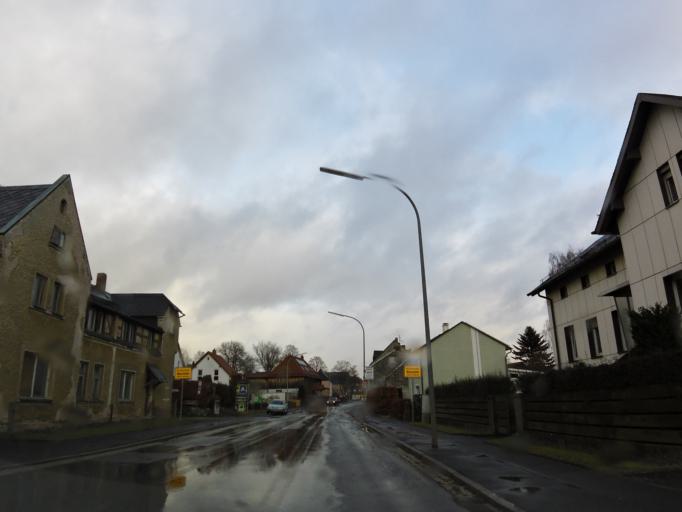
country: DE
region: Bavaria
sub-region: Upper Franconia
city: Wunsiedel
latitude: 50.0439
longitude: 12.0240
